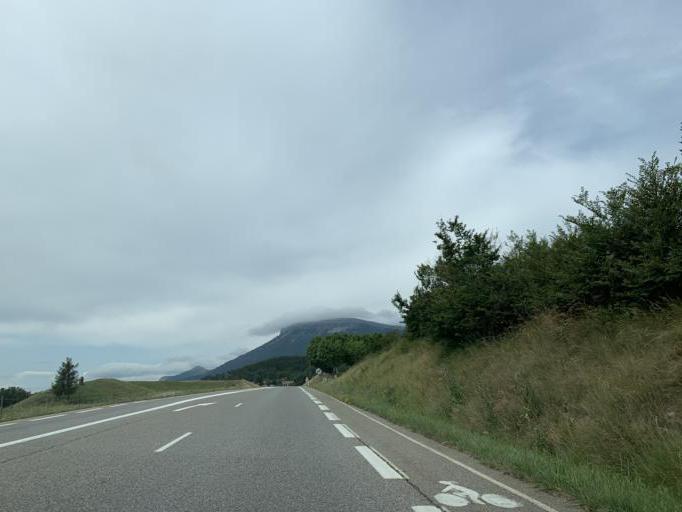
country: FR
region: Provence-Alpes-Cote d'Azur
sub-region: Departement des Hautes-Alpes
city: Gap
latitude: 44.5516
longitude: 6.0308
